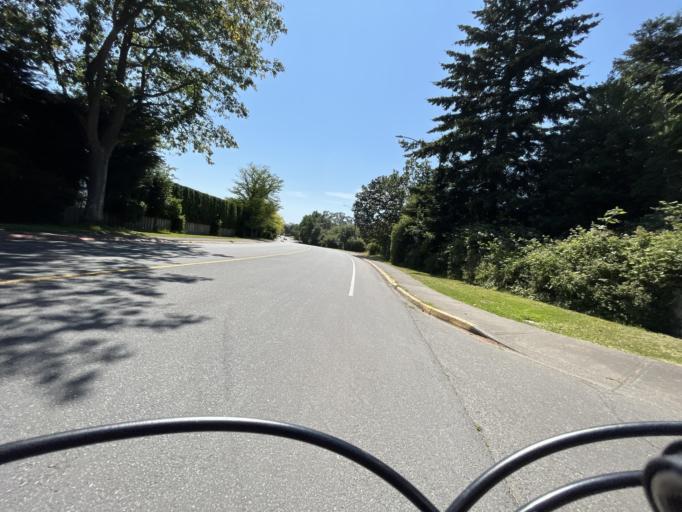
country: CA
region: British Columbia
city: Oak Bay
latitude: 48.4496
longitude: -123.3183
